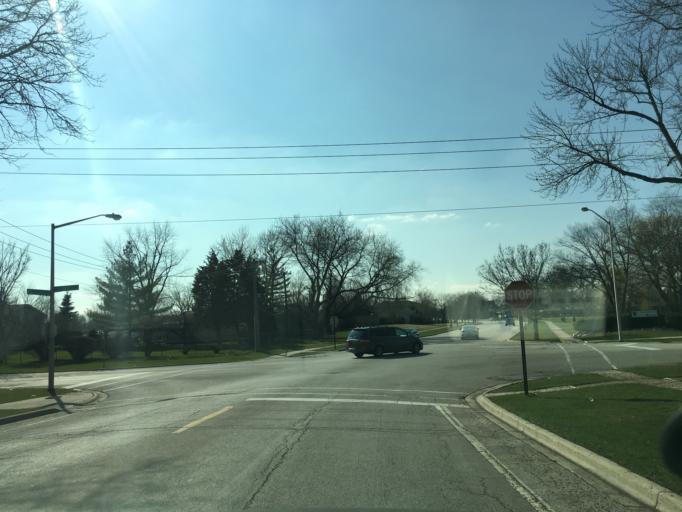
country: US
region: Illinois
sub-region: DuPage County
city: Hanover Park
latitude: 42.0182
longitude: -88.1286
